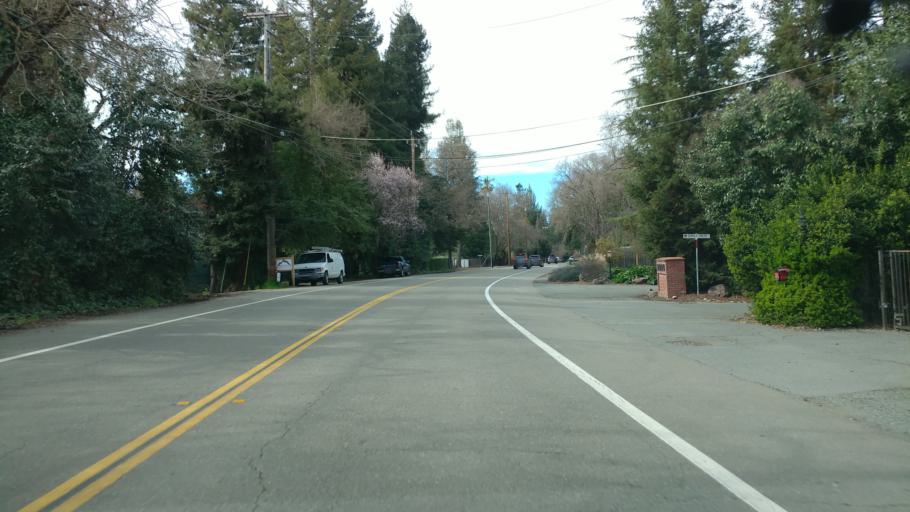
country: US
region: California
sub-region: Contra Costa County
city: Danville
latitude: 37.8315
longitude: -122.0131
